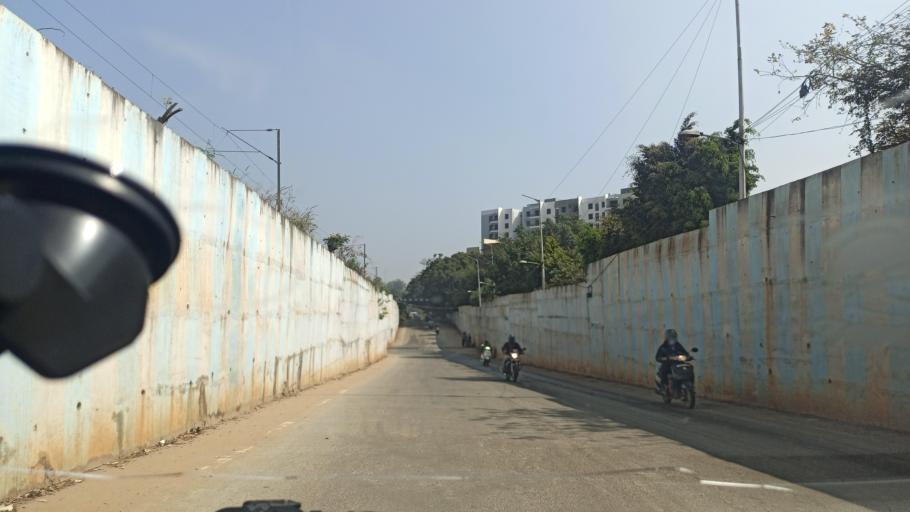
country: IN
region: Karnataka
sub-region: Bangalore Urban
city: Yelahanka
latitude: 13.0691
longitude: 77.5852
